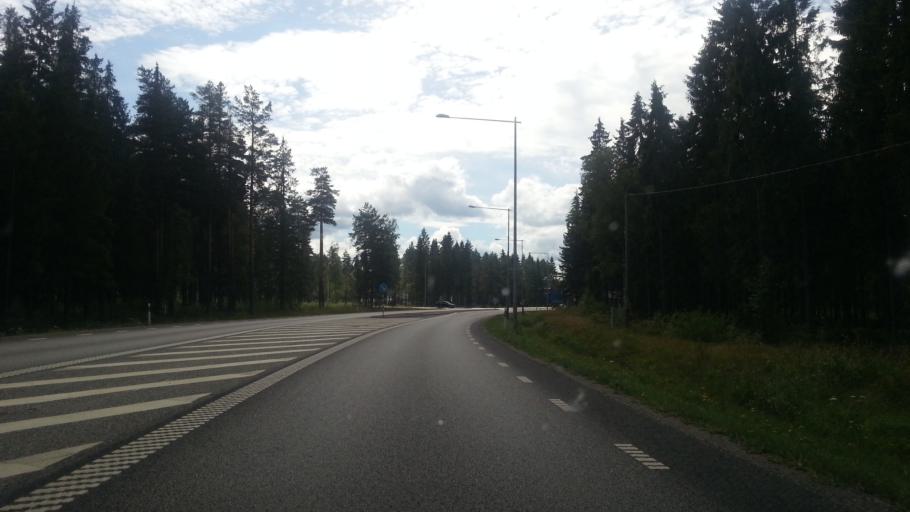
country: SE
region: OErebro
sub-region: Lindesbergs Kommun
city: Lindesberg
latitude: 59.6192
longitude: 15.1892
